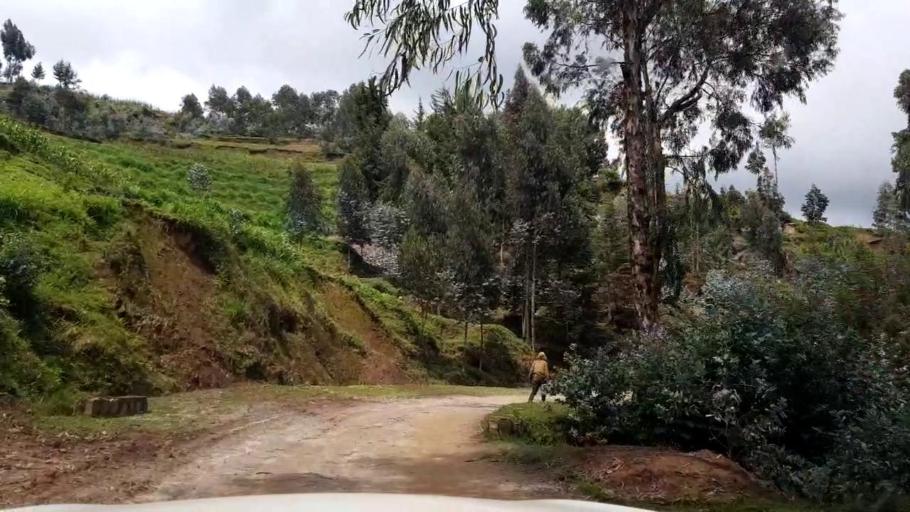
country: RW
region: Western Province
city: Kibuye
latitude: -1.9228
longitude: 29.4542
